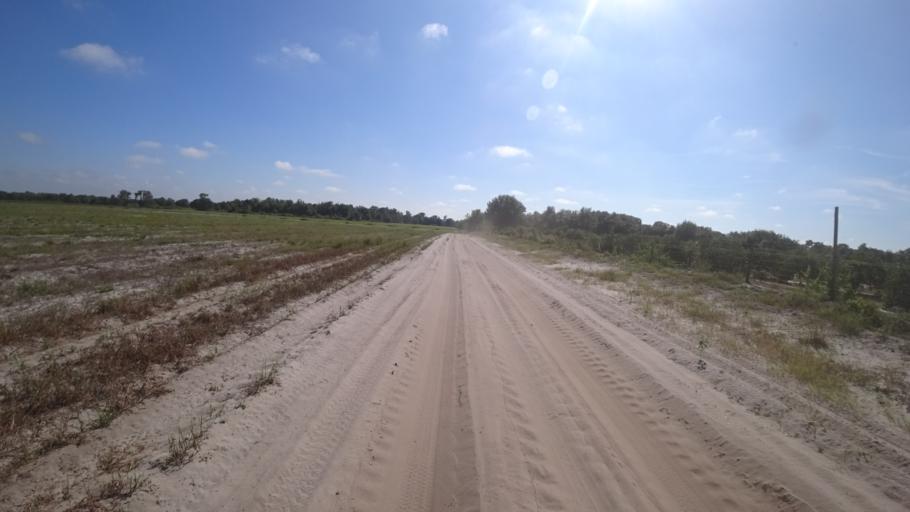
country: US
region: Florida
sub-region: DeSoto County
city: Arcadia
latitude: 27.2959
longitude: -82.0518
